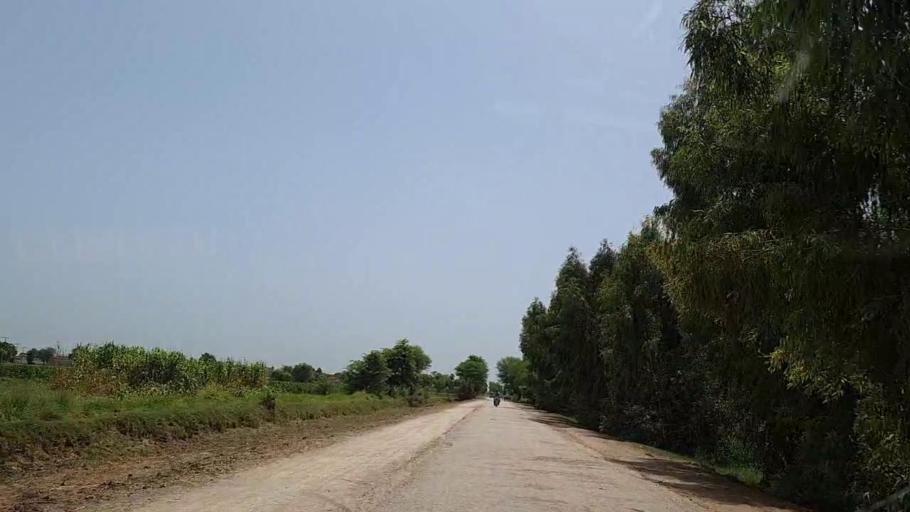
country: PK
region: Sindh
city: Tharu Shah
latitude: 26.9663
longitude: 68.0468
